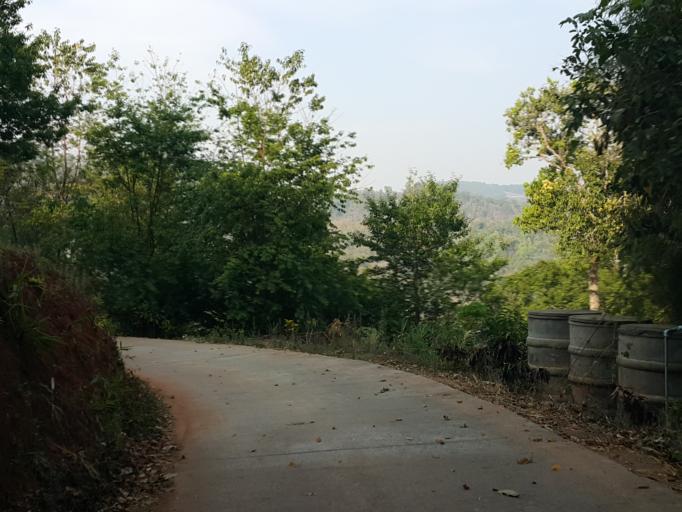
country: TH
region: Chiang Mai
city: Samoeng
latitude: 18.9104
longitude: 98.7975
